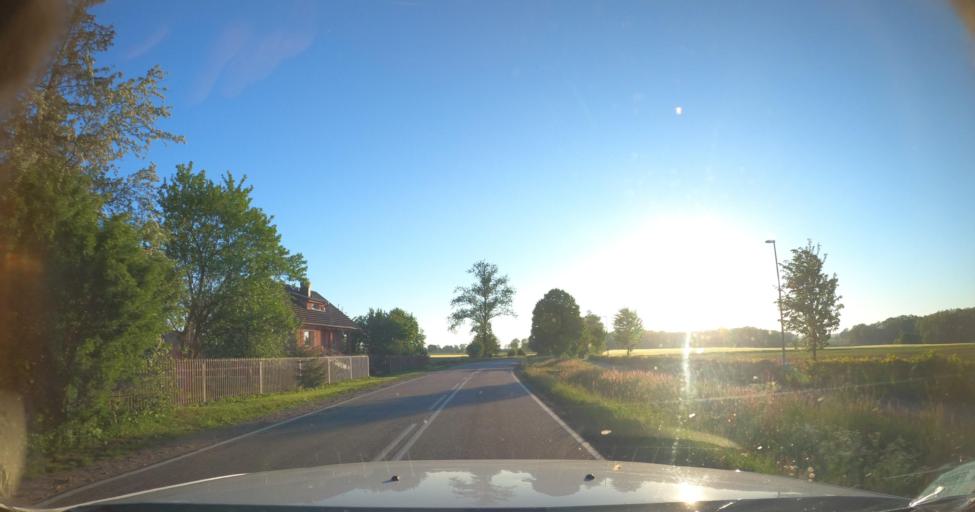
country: PL
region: Pomeranian Voivodeship
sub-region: Powiat slupski
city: Potegowo
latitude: 54.4177
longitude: 17.4006
